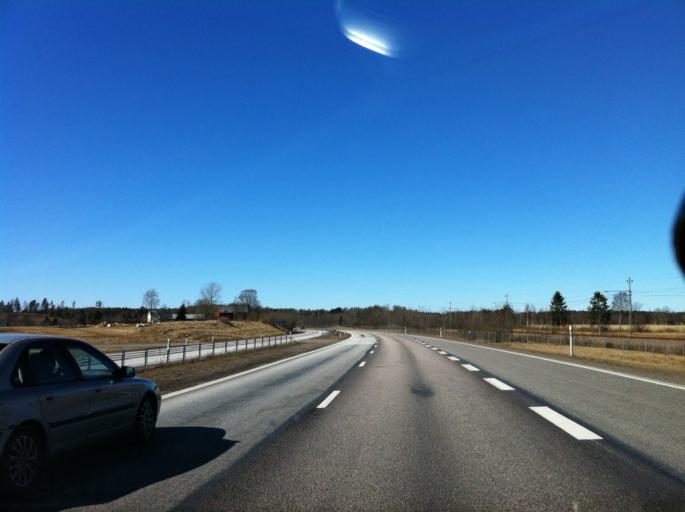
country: SE
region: Vaestra Goetaland
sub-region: Vanersborgs Kommun
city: Vanersborg
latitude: 58.3731
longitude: 12.3443
